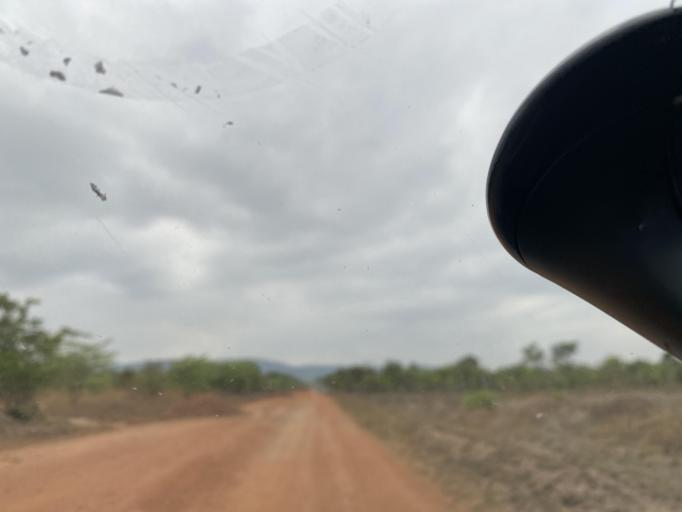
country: ZM
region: Lusaka
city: Chongwe
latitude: -15.2103
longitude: 28.7572
